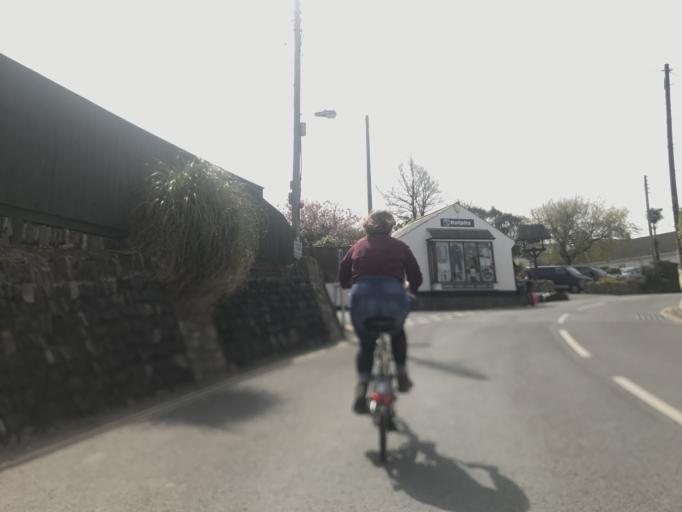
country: GB
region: England
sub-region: Devon
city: Braunton
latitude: 51.1300
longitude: -4.2245
